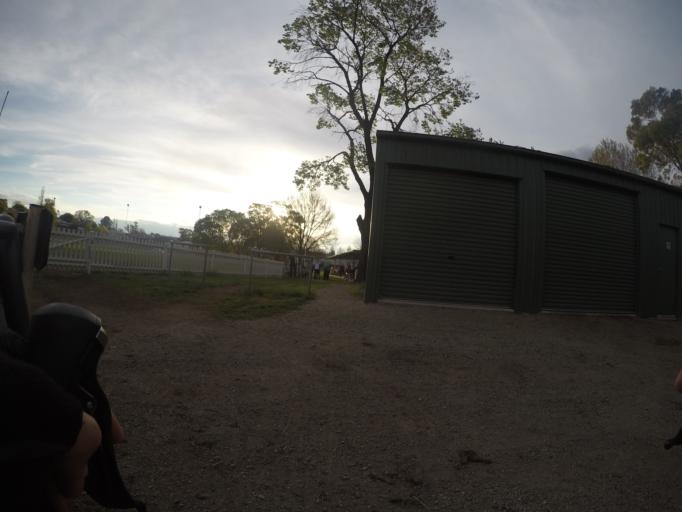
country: AU
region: New South Wales
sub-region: Cabonne
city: Molong
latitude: -33.0884
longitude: 148.8683
